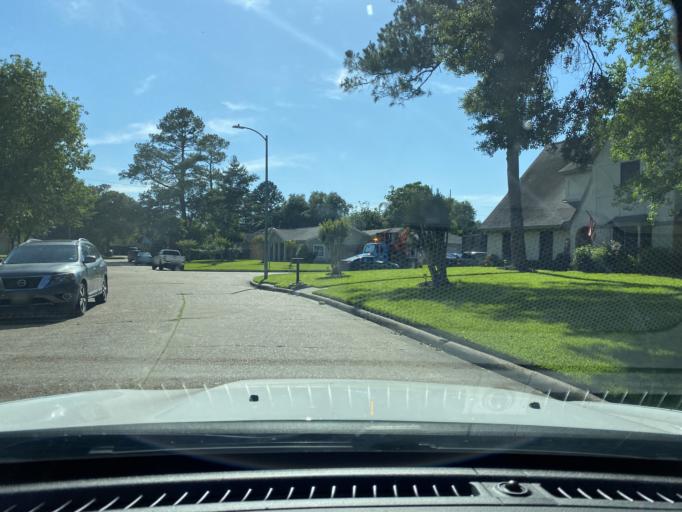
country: US
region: Texas
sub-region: Harris County
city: Hudson
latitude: 29.8764
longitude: -95.4853
